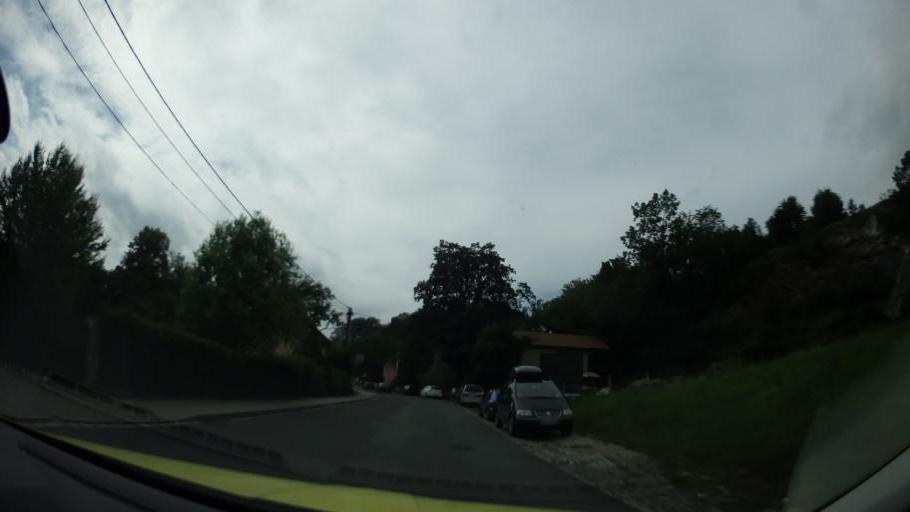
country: CZ
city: Stramberk
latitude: 49.5862
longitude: 18.1285
